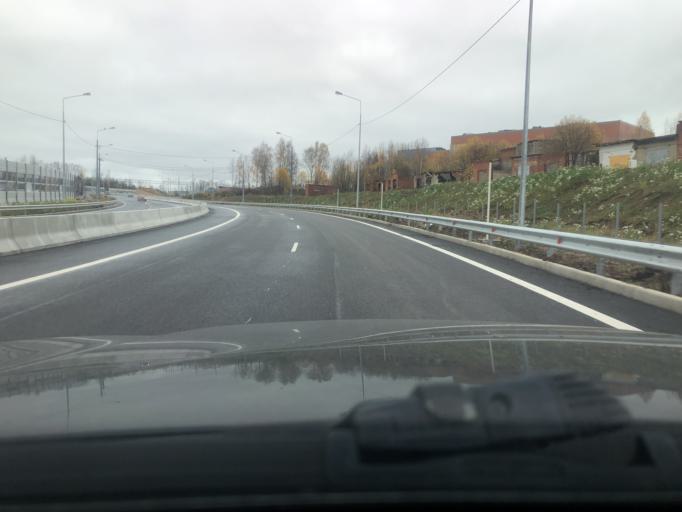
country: RU
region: Moskovskaya
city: Sergiyev Posad
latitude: 56.3377
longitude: 38.1215
